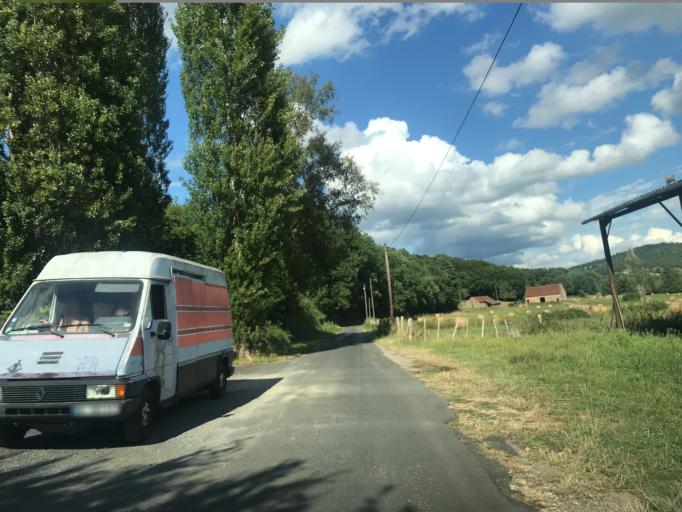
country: FR
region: Aquitaine
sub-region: Departement de la Dordogne
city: Rouffignac-Saint-Cernin-de-Reilhac
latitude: 44.9776
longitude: 1.0362
